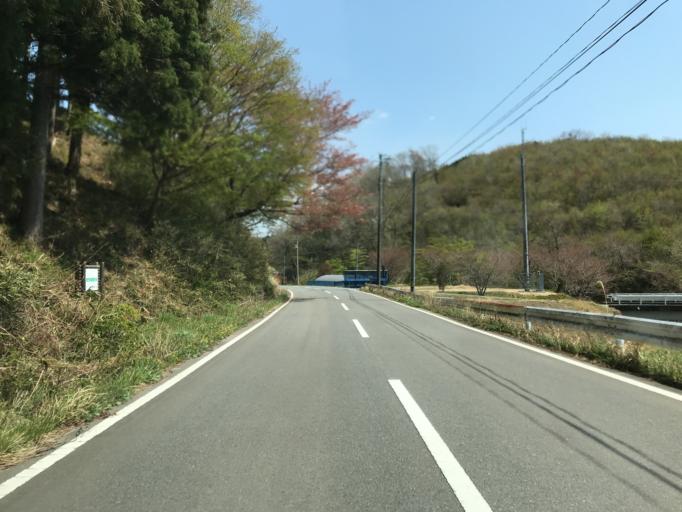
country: JP
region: Ibaraki
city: Kitaibaraki
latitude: 36.9570
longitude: 140.6719
